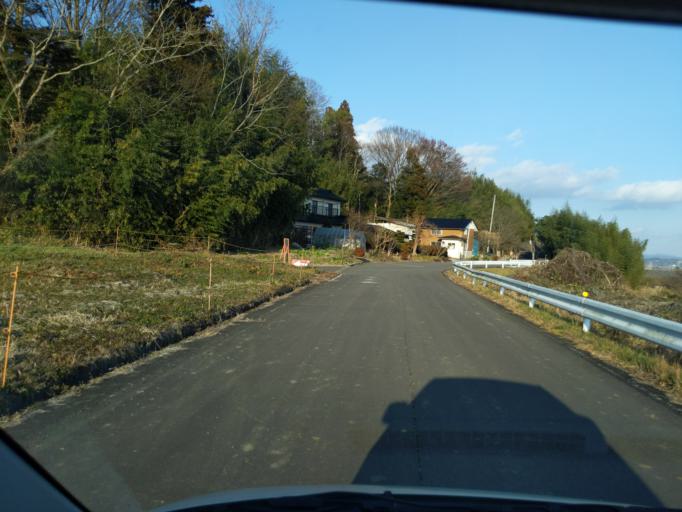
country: JP
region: Miyagi
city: Wakuya
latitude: 38.7090
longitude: 141.1409
